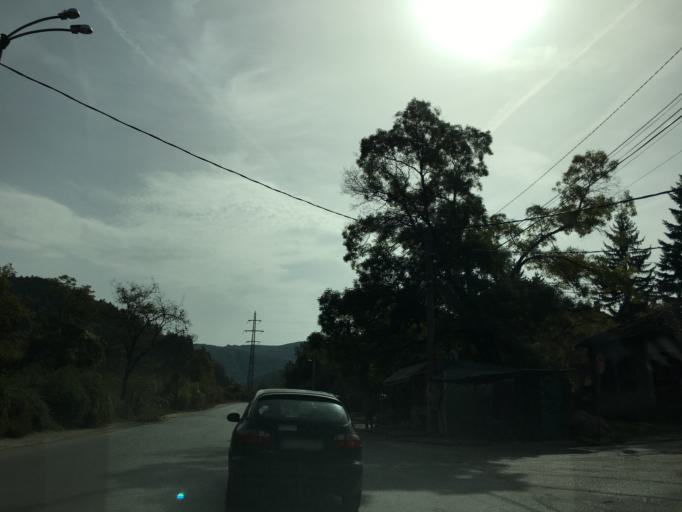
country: BG
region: Sofia-Capital
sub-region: Stolichna Obshtina
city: Sofia
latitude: 42.5825
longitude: 23.4242
